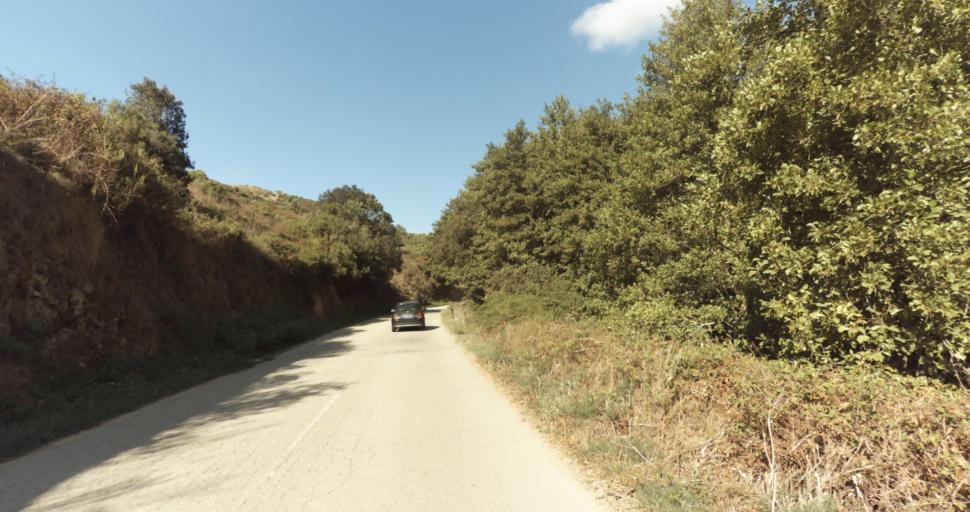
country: FR
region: Corsica
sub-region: Departement de la Corse-du-Sud
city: Ajaccio
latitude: 41.9331
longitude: 8.6885
